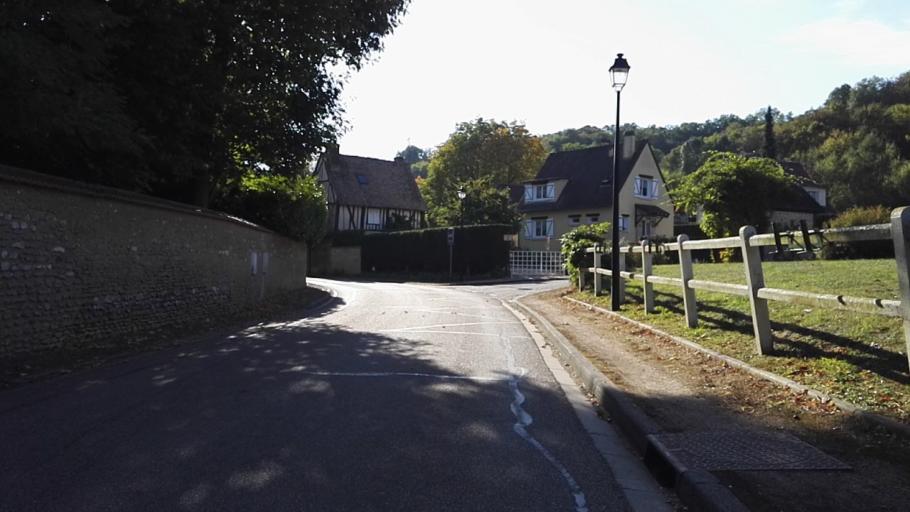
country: FR
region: Haute-Normandie
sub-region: Departement de l'Eure
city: Menilles
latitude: 49.0300
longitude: 1.3438
